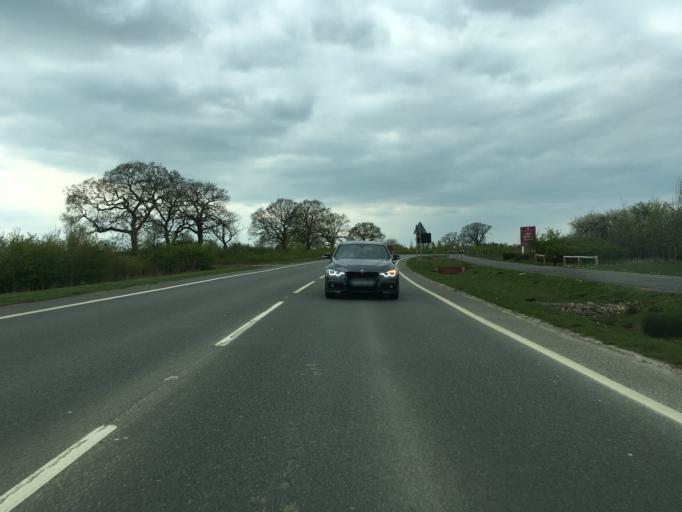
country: GB
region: England
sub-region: Oxfordshire
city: Bicester
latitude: 51.8875
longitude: -1.1732
